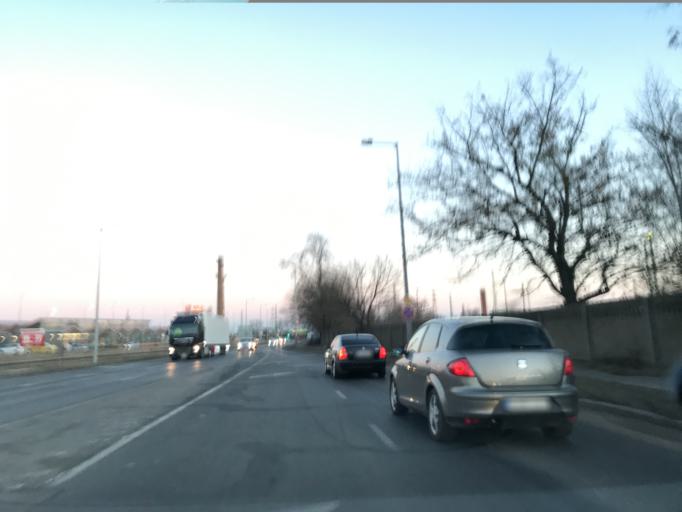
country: HU
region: Gyor-Moson-Sopron
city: Gyor
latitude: 47.6873
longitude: 17.6471
